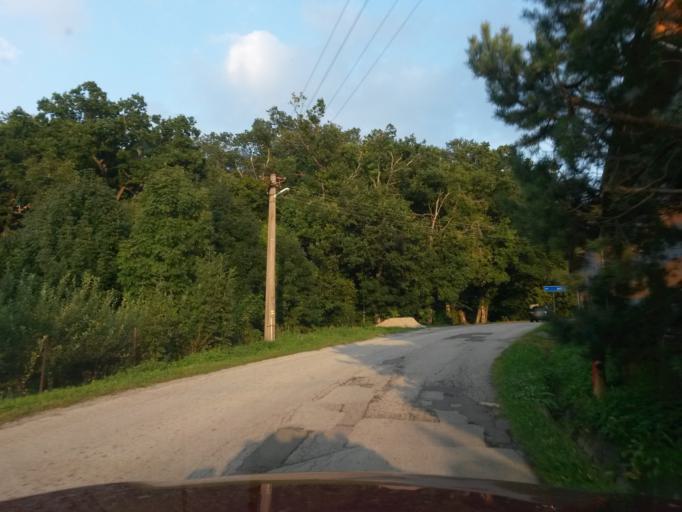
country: SK
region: Kosicky
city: Secovce
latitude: 48.7993
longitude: 21.4794
